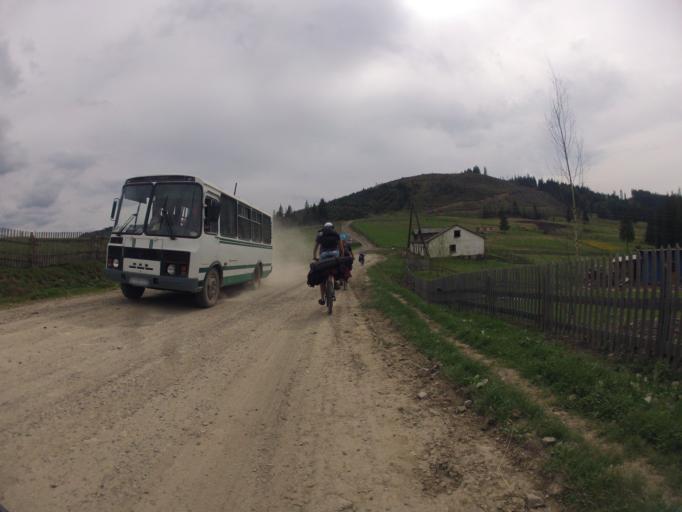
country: UA
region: Chernivtsi
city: Putyla
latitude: 47.8894
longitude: 25.1657
